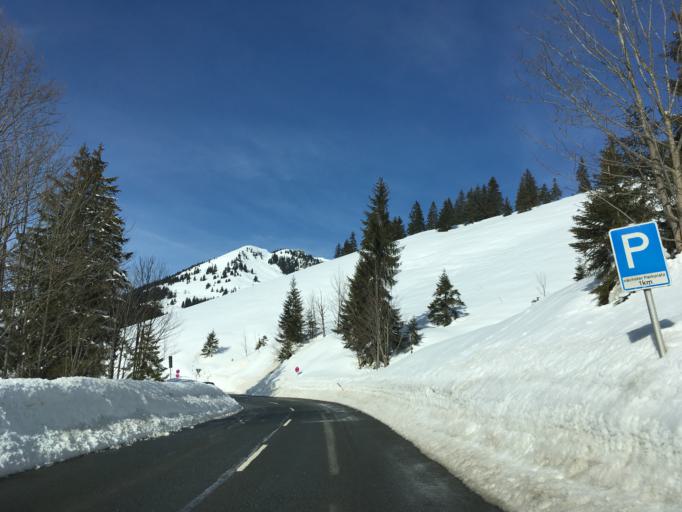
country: DE
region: Bavaria
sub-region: Upper Bavaria
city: Bayrischzell
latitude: 47.6836
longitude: 12.0464
